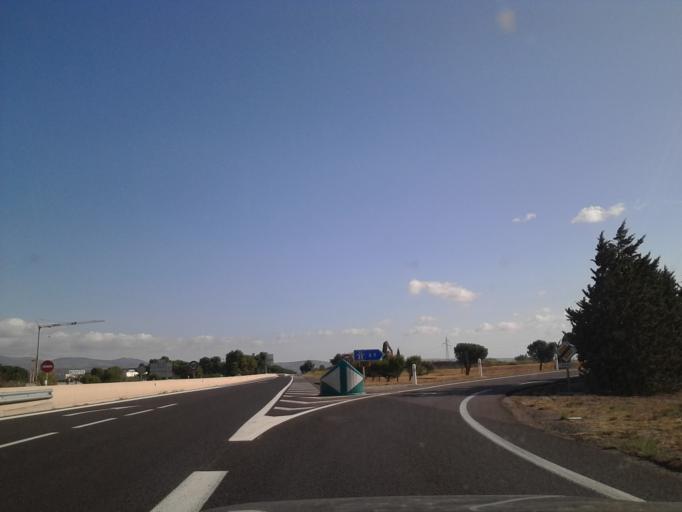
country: FR
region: Languedoc-Roussillon
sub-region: Departement des Pyrenees-Orientales
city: Rivesaltes
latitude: 42.7795
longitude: 2.9036
